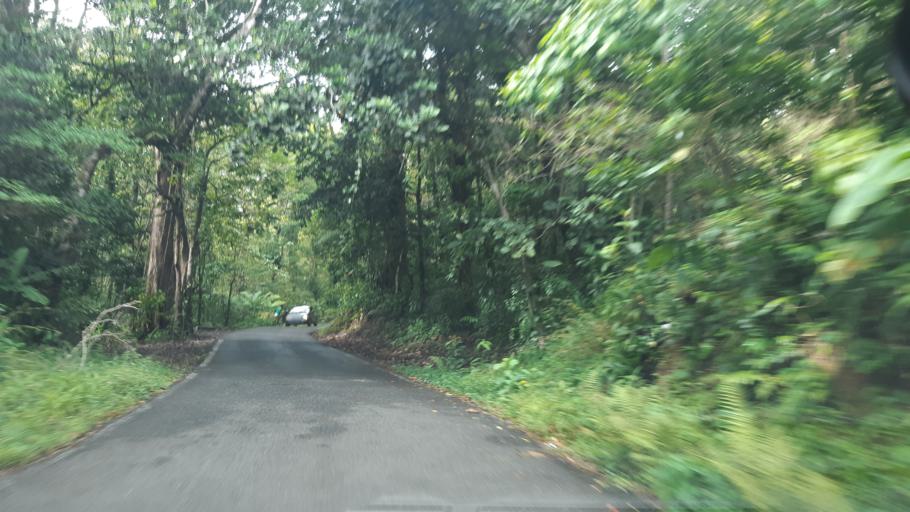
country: GP
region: Guadeloupe
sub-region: Guadeloupe
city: Saint-Claude
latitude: 16.0320
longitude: -61.6771
